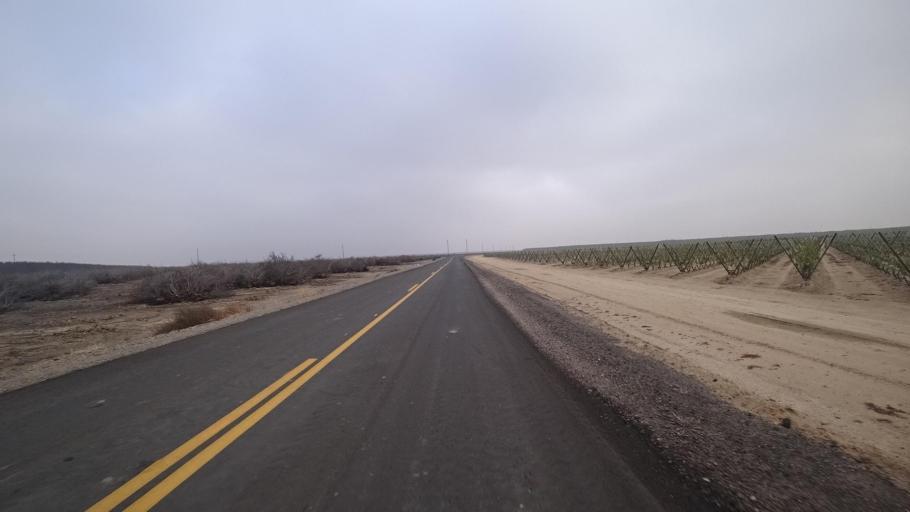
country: US
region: California
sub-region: Kern County
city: Maricopa
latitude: 35.1151
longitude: -119.3531
